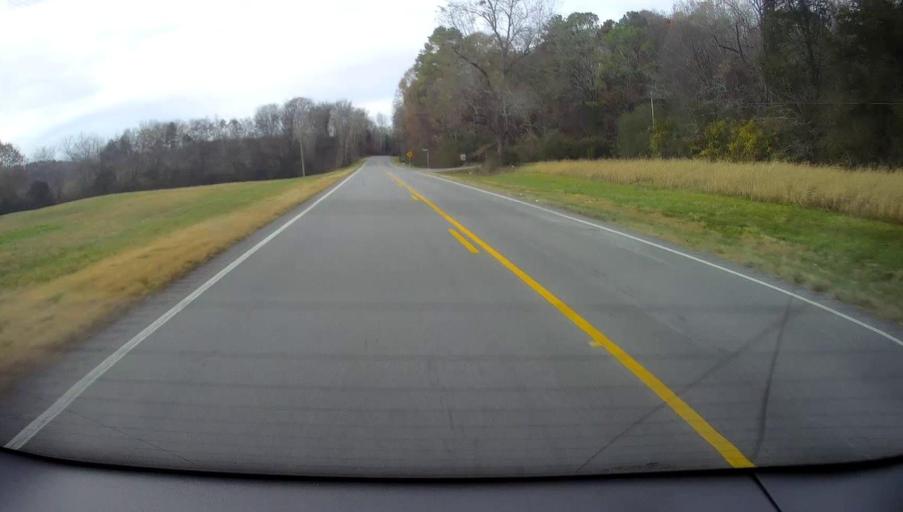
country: US
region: Alabama
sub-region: Marshall County
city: Arab
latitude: 34.3737
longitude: -86.6502
